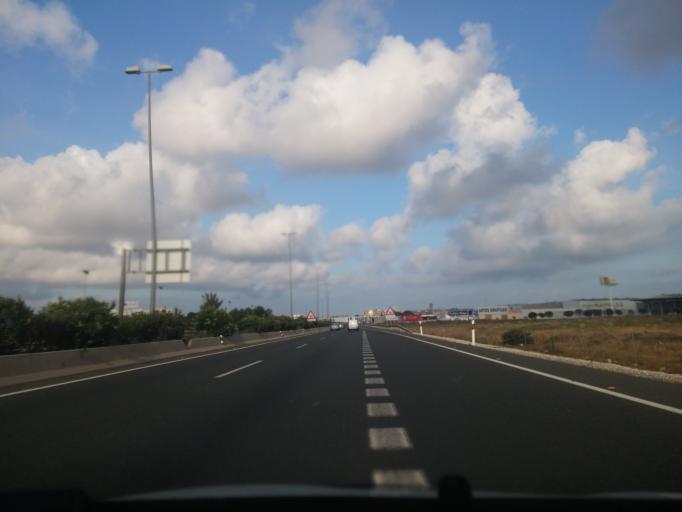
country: ES
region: Valencia
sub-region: Provincia de Alicante
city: San Vicent del Raspeig
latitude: 38.3797
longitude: -0.5083
